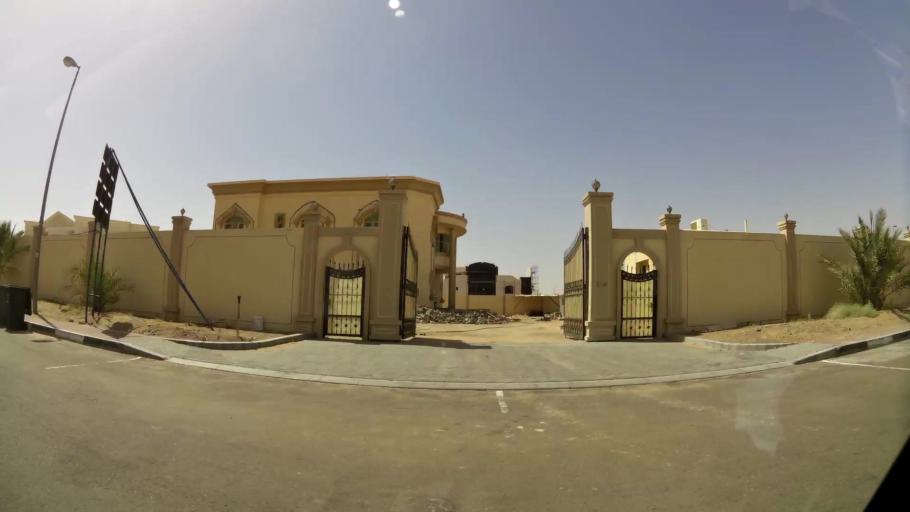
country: OM
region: Al Buraimi
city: Al Buraymi
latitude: 24.3002
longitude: 55.7500
